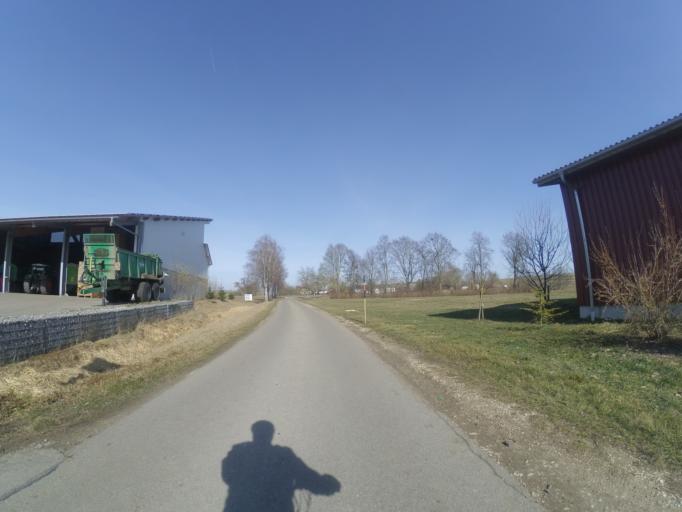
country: DE
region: Baden-Wuerttemberg
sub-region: Tuebingen Region
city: Ollingen
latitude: 48.5020
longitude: 10.1448
